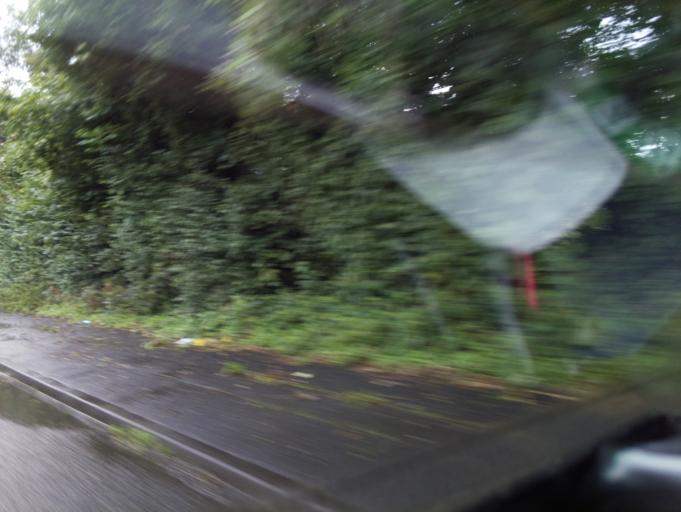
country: GB
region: England
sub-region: Devon
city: South Brent
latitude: 50.4205
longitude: -3.8357
